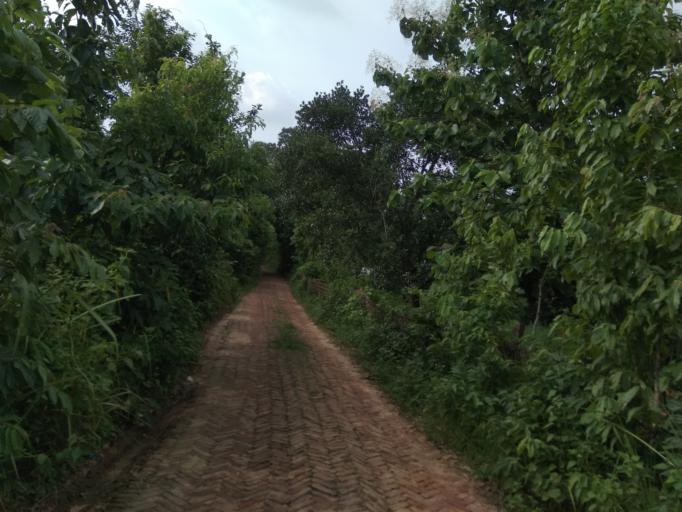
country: BD
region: Chittagong
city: Manikchari
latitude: 22.9282
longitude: 91.9128
